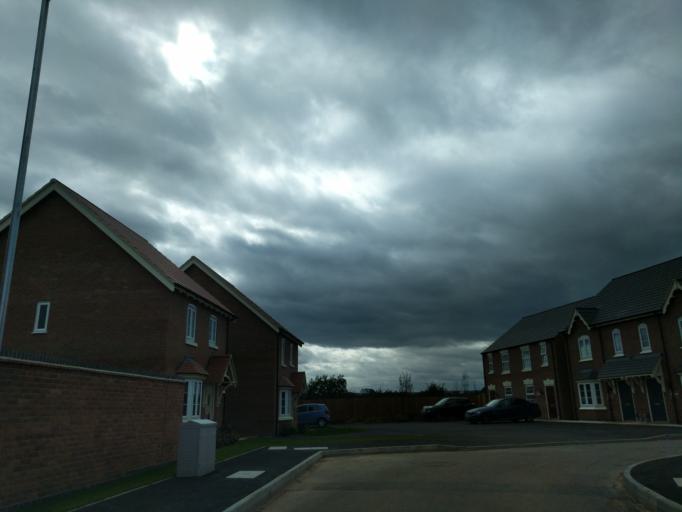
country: GB
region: England
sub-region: Leicestershire
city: Kirby Muxloe
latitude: 52.6152
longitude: -1.2210
